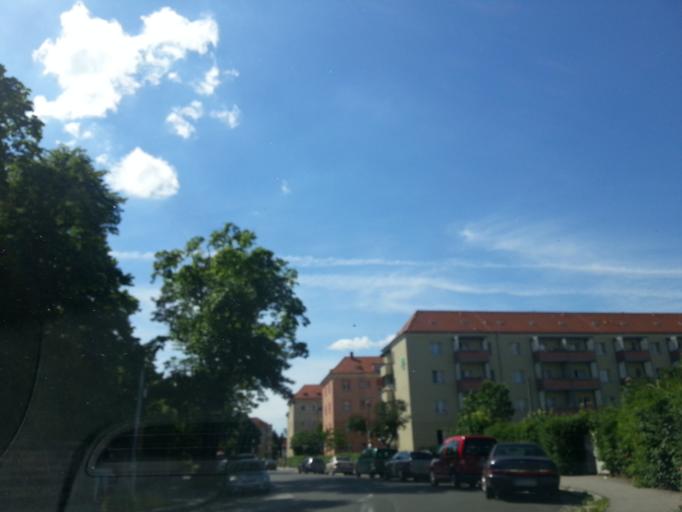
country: DE
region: Saxony
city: Dresden
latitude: 51.0867
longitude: 13.7217
